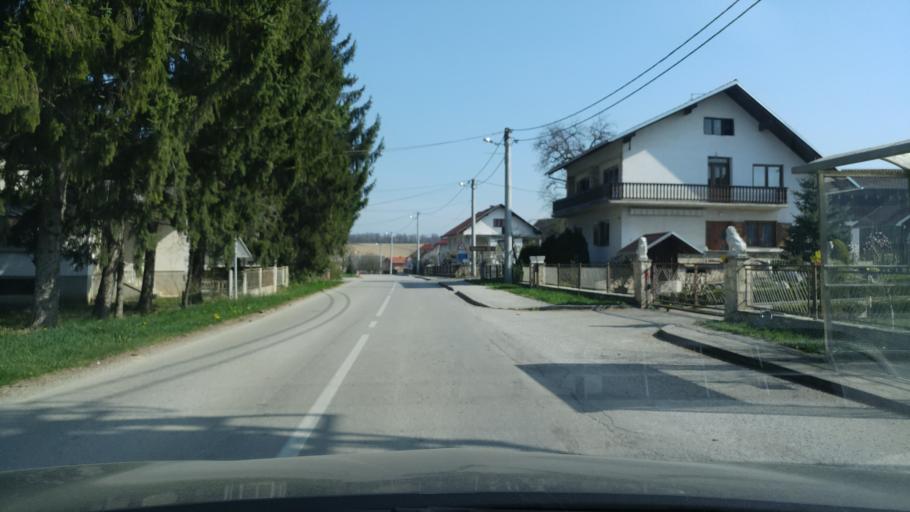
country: HR
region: Zagrebacka
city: Pojatno
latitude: 45.9605
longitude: 15.7356
